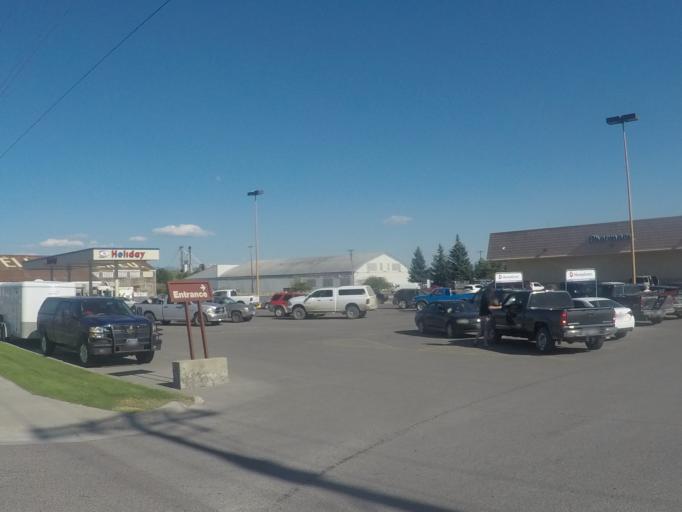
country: US
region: Montana
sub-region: Flathead County
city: Kalispell
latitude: 48.2004
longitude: -114.3294
